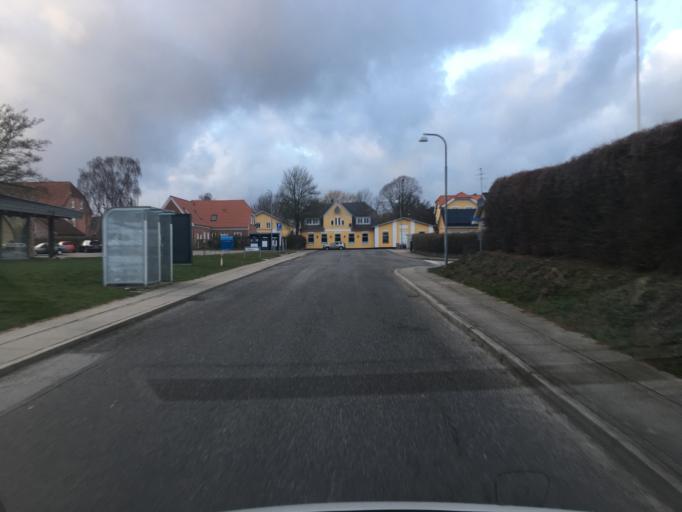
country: DK
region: South Denmark
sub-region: Aabenraa Kommune
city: Aabenraa
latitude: 54.9787
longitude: 9.4998
